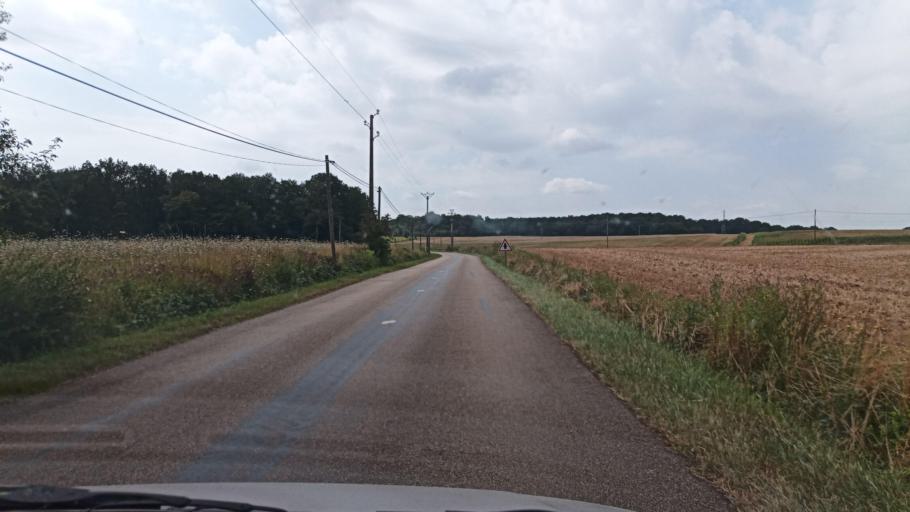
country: FR
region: Centre
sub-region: Departement du Loiret
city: Courtenay
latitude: 48.0053
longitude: 3.1512
